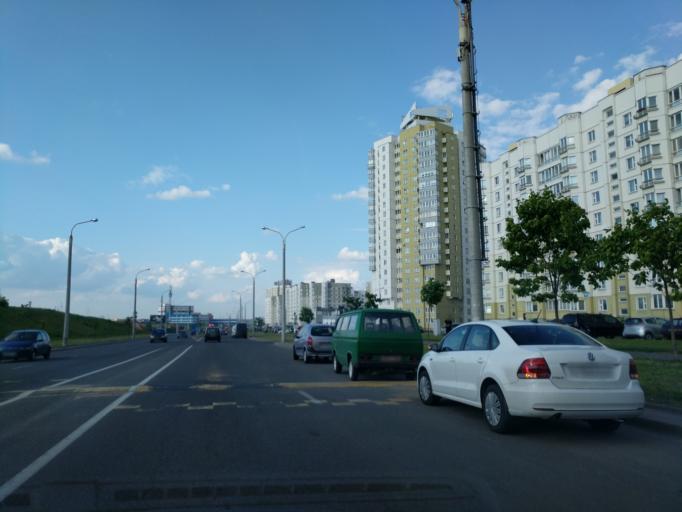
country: BY
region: Minsk
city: Zhdanovichy
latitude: 53.9276
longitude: 27.4230
